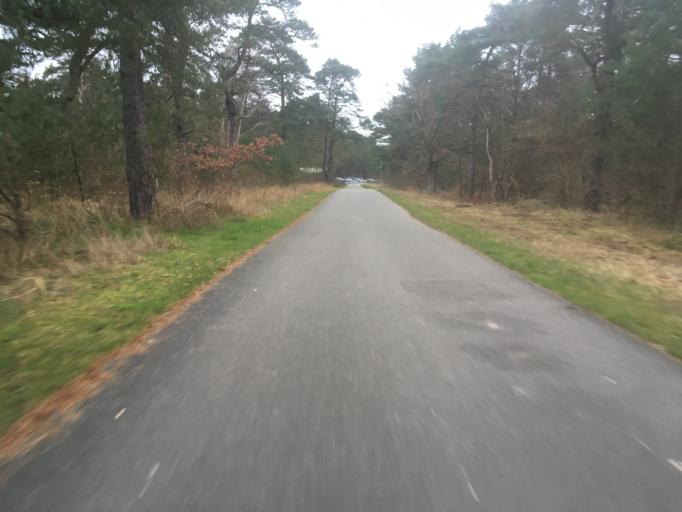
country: DE
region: Mecklenburg-Vorpommern
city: Sagard
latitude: 54.4645
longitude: 13.5663
